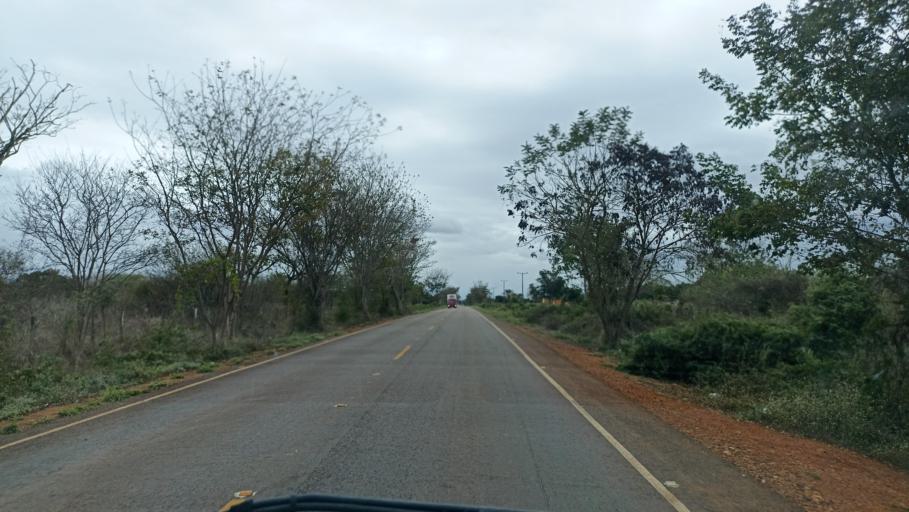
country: BR
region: Bahia
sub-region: Andarai
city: Vera Cruz
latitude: -12.9776
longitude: -41.0187
